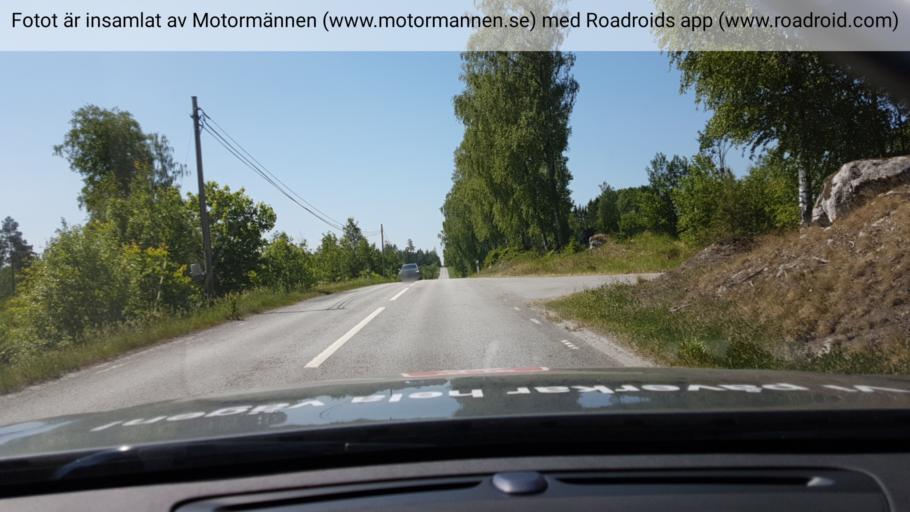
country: SE
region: Stockholm
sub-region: Norrtalje Kommun
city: Rimbo
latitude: 59.7717
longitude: 18.4295
